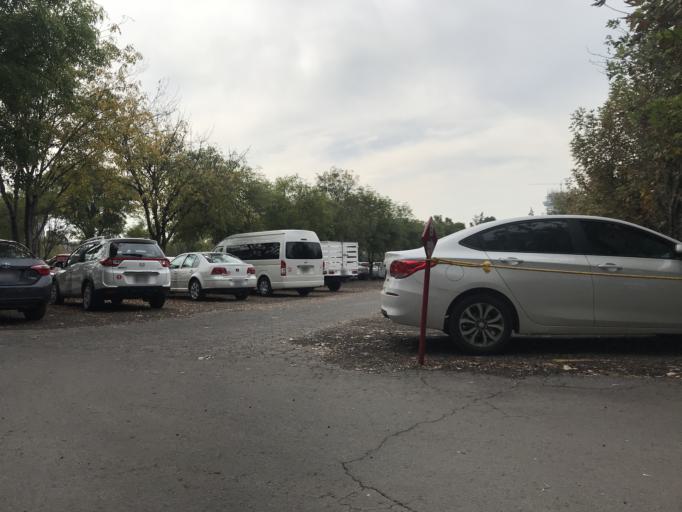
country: MX
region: Puebla
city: Tlazcalancingo
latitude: 19.0314
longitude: -98.2433
